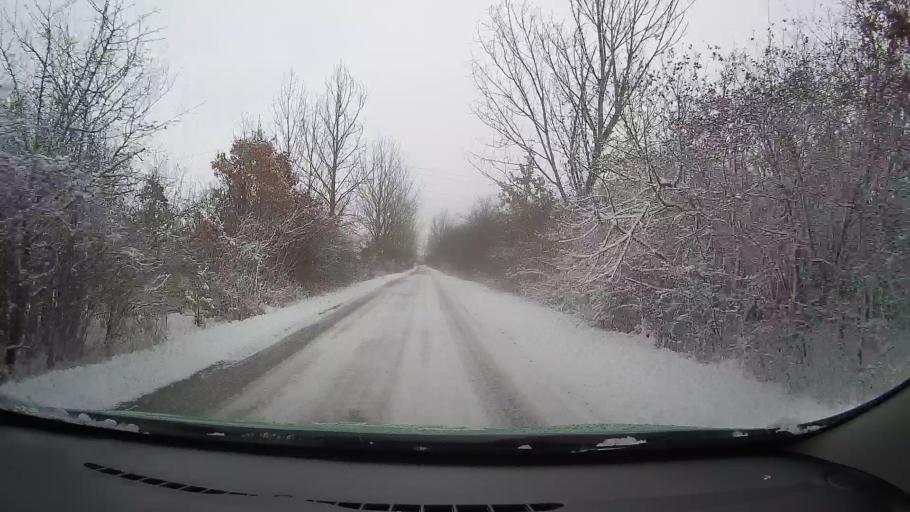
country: RO
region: Hunedoara
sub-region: Municipiul Hunedoara
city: Pestisu Mare
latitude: 45.8085
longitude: 22.9109
